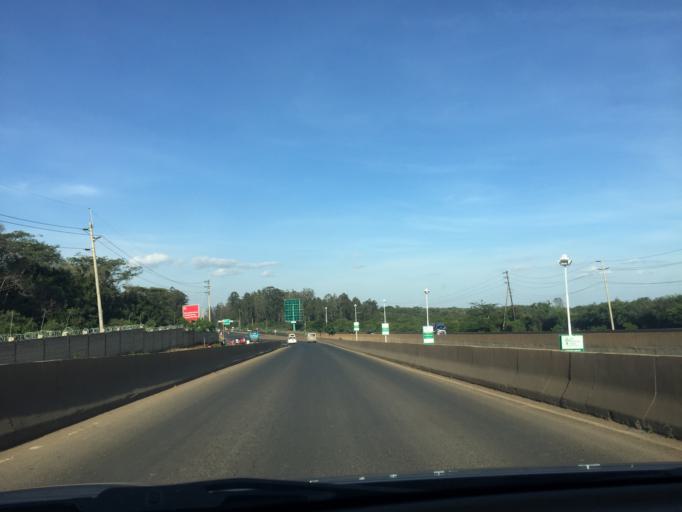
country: KE
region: Nairobi Area
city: Nairobi
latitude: -1.3423
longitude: 36.7673
